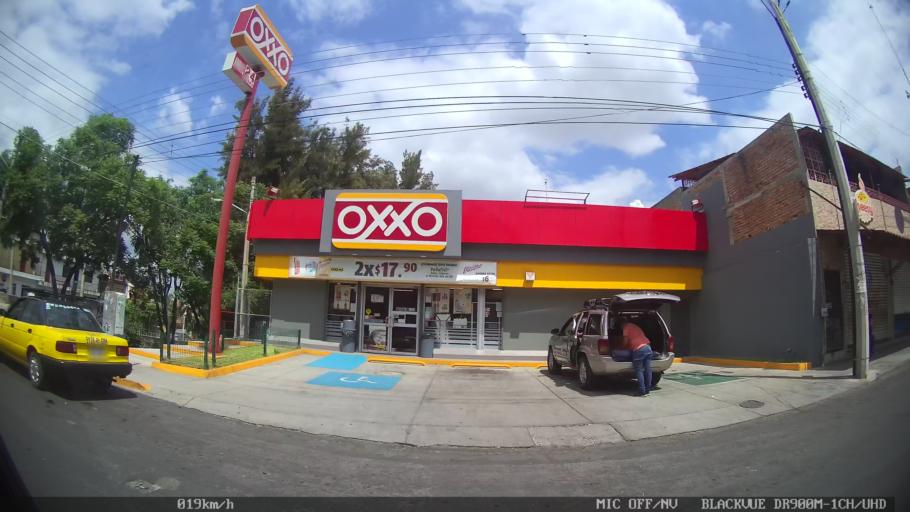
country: MX
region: Jalisco
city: Tonala
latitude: 20.6311
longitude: -103.2521
